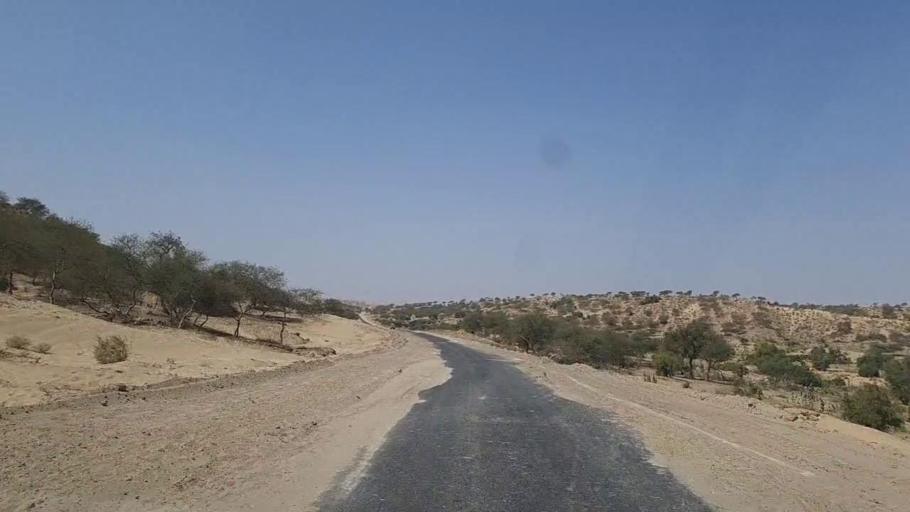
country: PK
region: Sindh
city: Diplo
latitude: 24.5883
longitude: 69.5462
